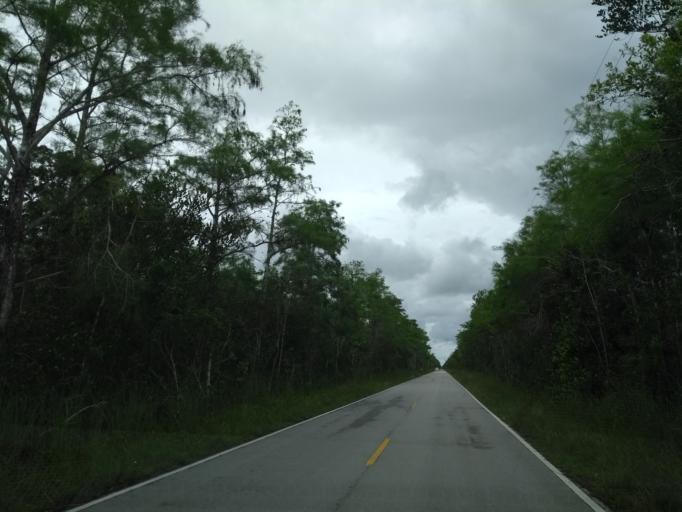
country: US
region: Florida
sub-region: Miami-Dade County
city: The Hammocks
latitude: 25.7613
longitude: -80.8900
